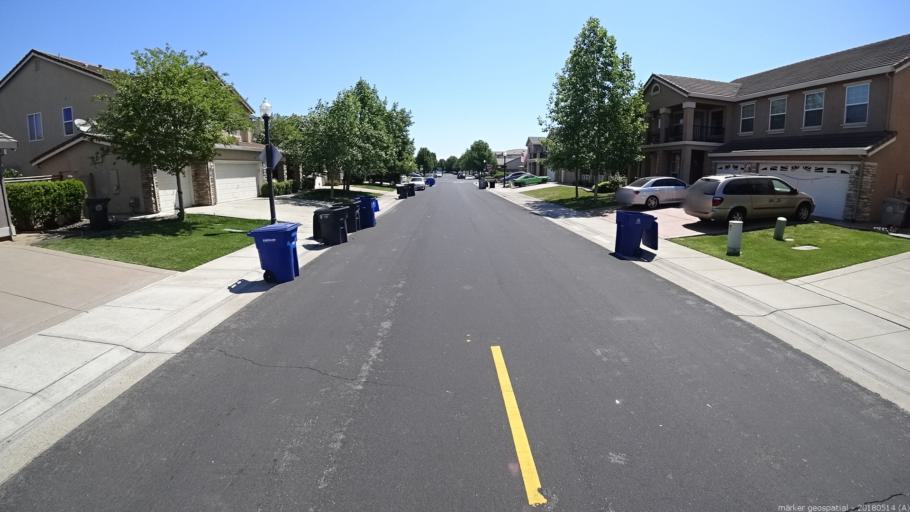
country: US
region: California
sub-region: Yolo County
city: West Sacramento
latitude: 38.6282
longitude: -121.5291
